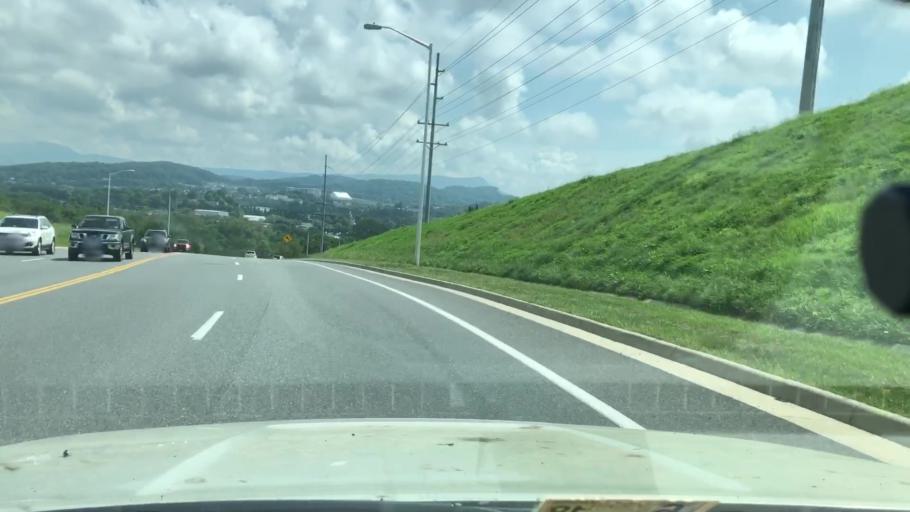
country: US
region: Virginia
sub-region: City of Harrisonburg
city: Harrisonburg
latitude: 38.4254
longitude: -78.8987
